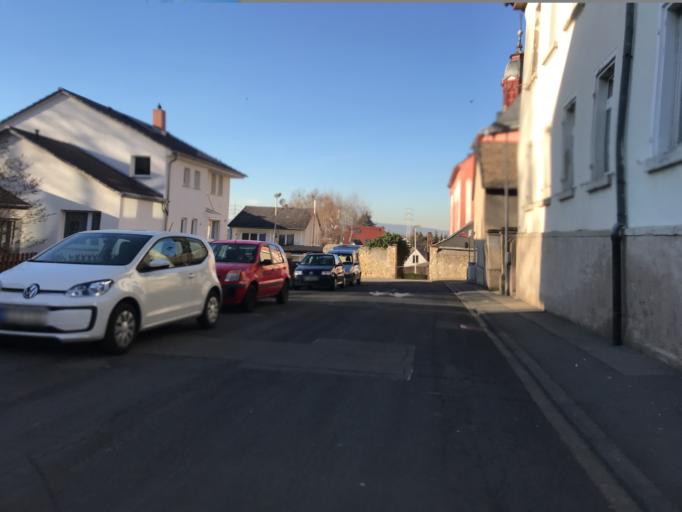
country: DE
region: Rheinland-Pfalz
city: Klein-Winternheim
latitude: 49.9591
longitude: 8.2286
